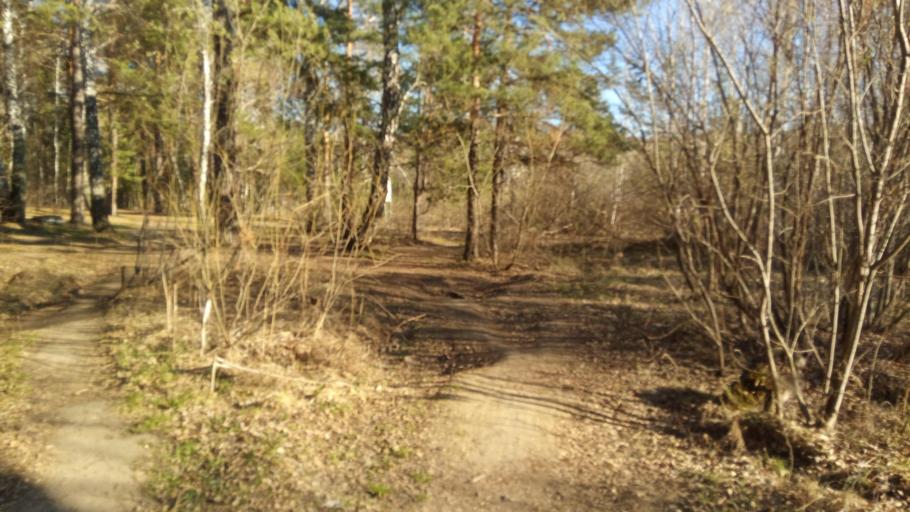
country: RU
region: Chelyabinsk
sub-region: Gorod Chelyabinsk
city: Chelyabinsk
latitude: 55.1419
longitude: 61.3308
